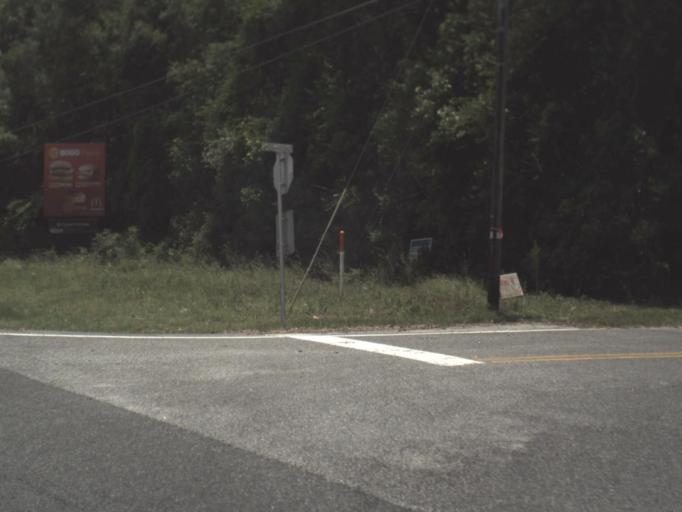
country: US
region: Florida
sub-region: Levy County
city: Manatee Road
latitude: 29.5706
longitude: -82.9126
